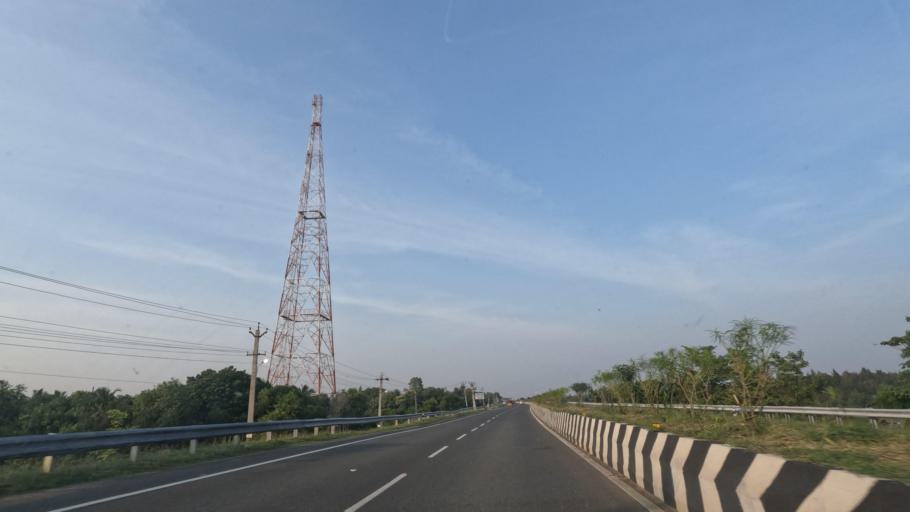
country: IN
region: Tamil Nadu
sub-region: Kancheepuram
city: Mamallapuram
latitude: 12.7099
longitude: 80.2247
